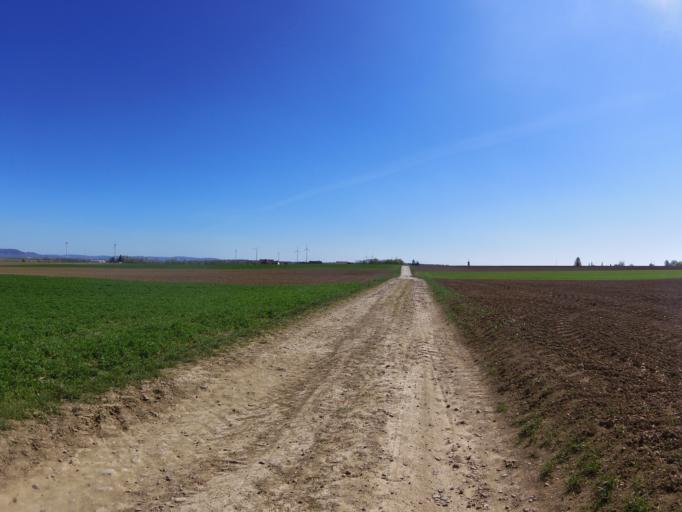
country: DE
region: Bavaria
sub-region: Regierungsbezirk Unterfranken
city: Biebelried
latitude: 49.8036
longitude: 10.0860
